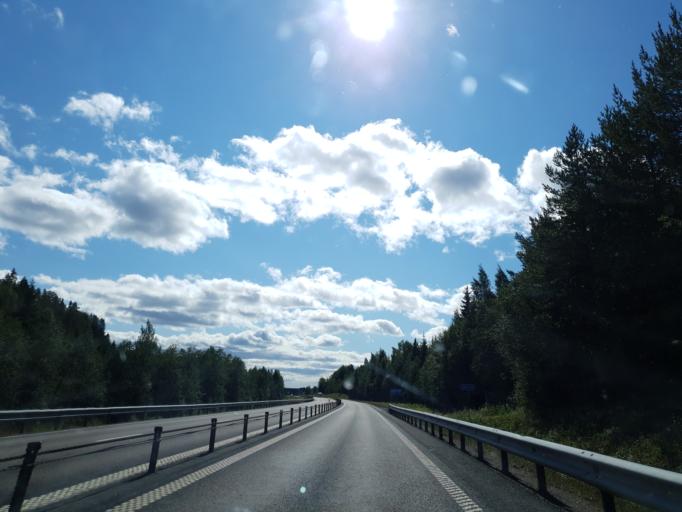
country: SE
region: Vaesternorrland
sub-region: OErnskoeldsviks Kommun
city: Husum
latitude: 63.4249
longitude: 19.2052
